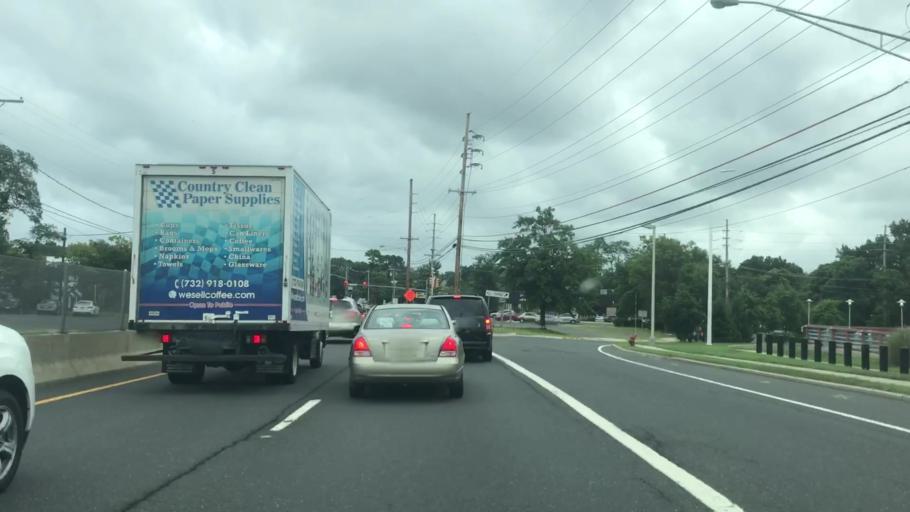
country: US
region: New Jersey
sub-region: Monmouth County
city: Eatontown
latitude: 40.2866
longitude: -74.0511
